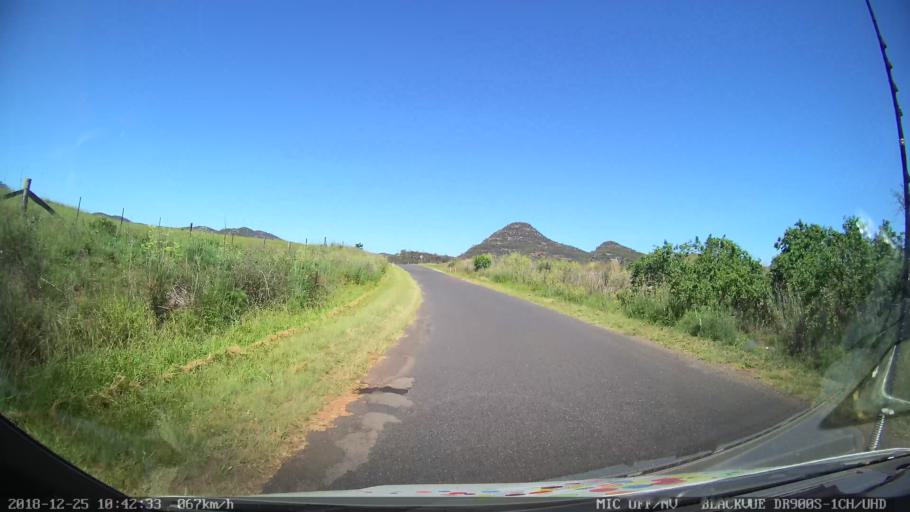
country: AU
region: New South Wales
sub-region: Upper Hunter Shire
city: Merriwa
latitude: -32.4164
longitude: 150.3220
